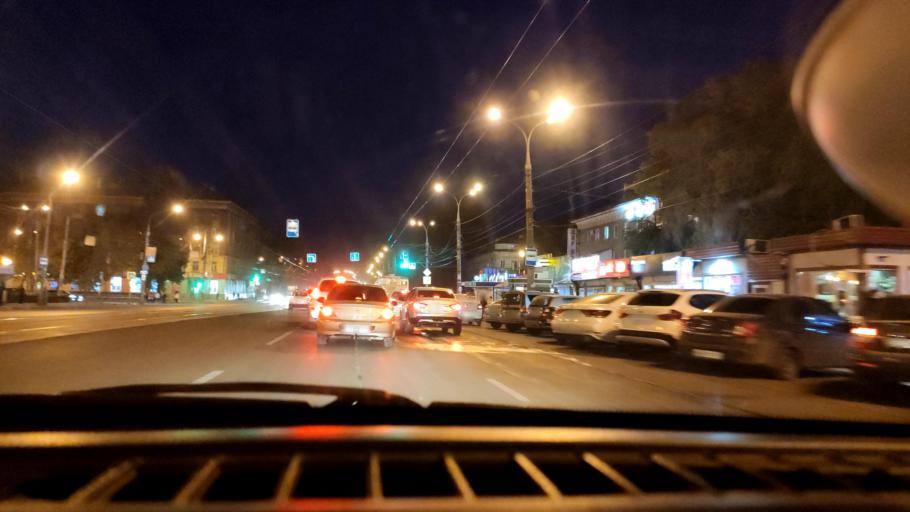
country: RU
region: Samara
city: Samara
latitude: 53.2188
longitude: 50.2635
